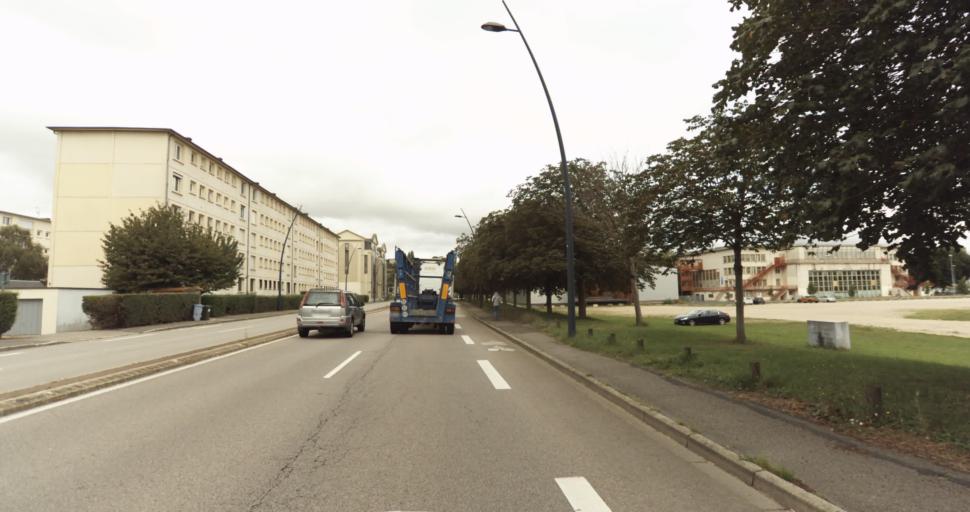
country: FR
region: Haute-Normandie
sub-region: Departement de l'Eure
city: Evreux
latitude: 49.0203
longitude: 1.1386
